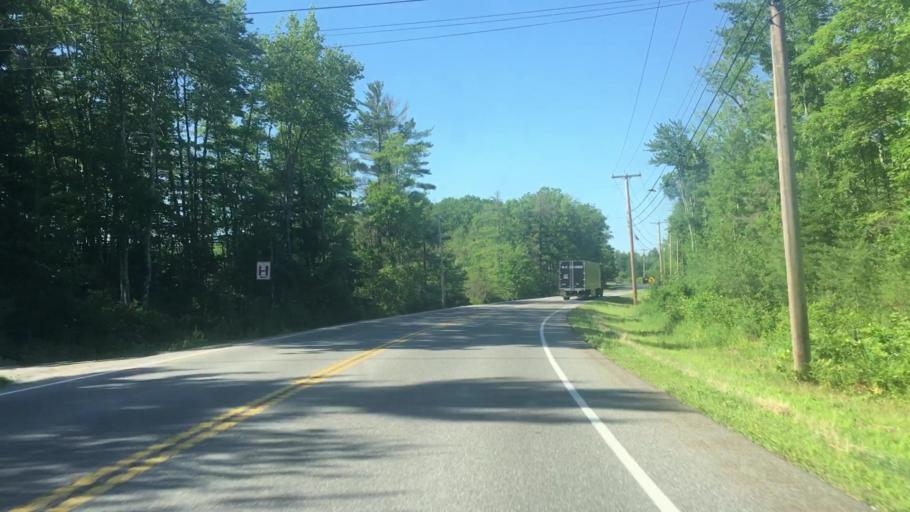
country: US
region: Maine
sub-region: York County
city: Dayton
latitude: 43.5592
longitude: -70.4987
